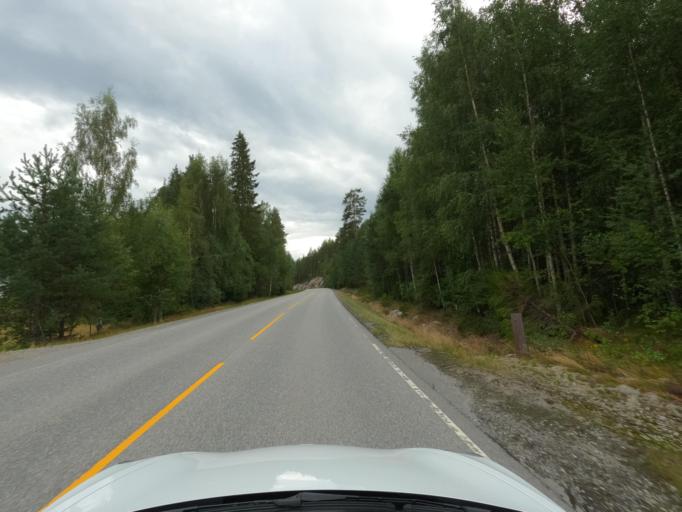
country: NO
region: Telemark
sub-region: Hjartdal
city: Sauland
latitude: 59.7277
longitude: 9.0193
